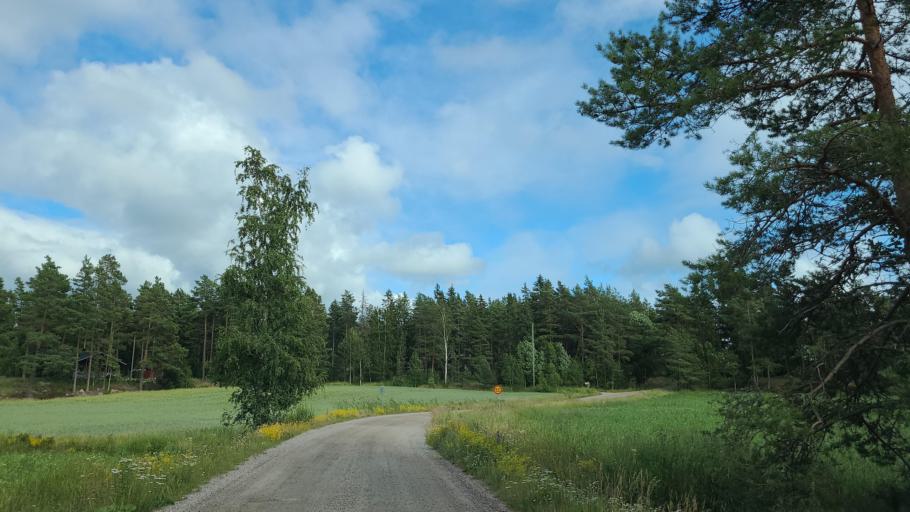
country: FI
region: Varsinais-Suomi
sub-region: Aboland-Turunmaa
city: Nagu
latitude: 60.1429
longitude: 21.7860
